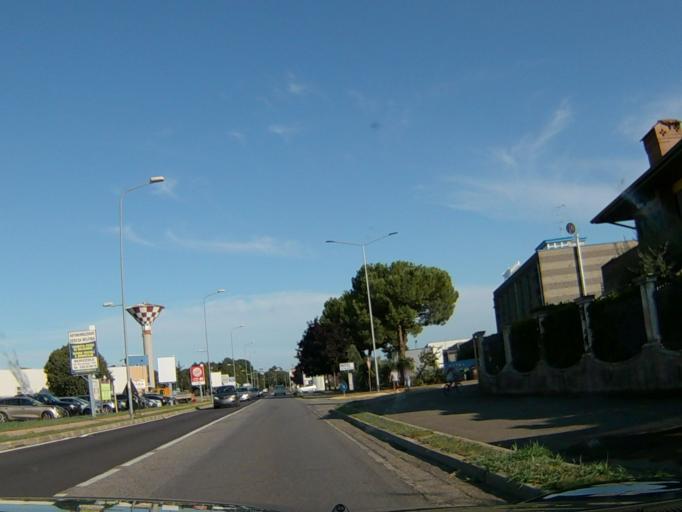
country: IT
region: Lombardy
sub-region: Provincia di Brescia
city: Molinetto
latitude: 45.4962
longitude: 10.3532
